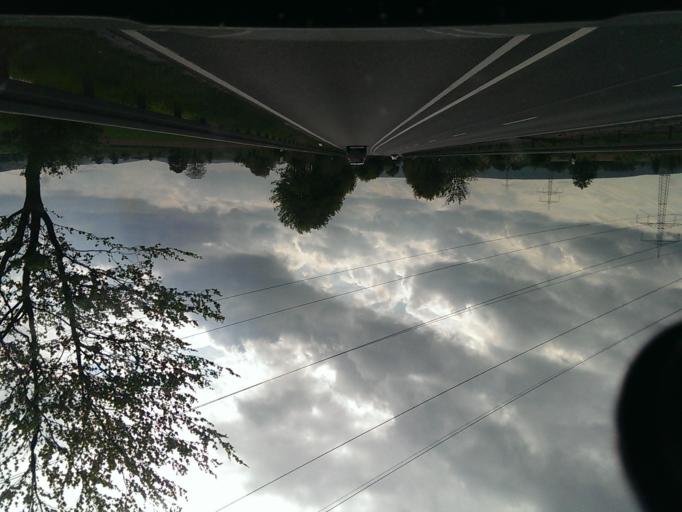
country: DE
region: Lower Saxony
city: Elze
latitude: 52.1297
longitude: 9.7273
